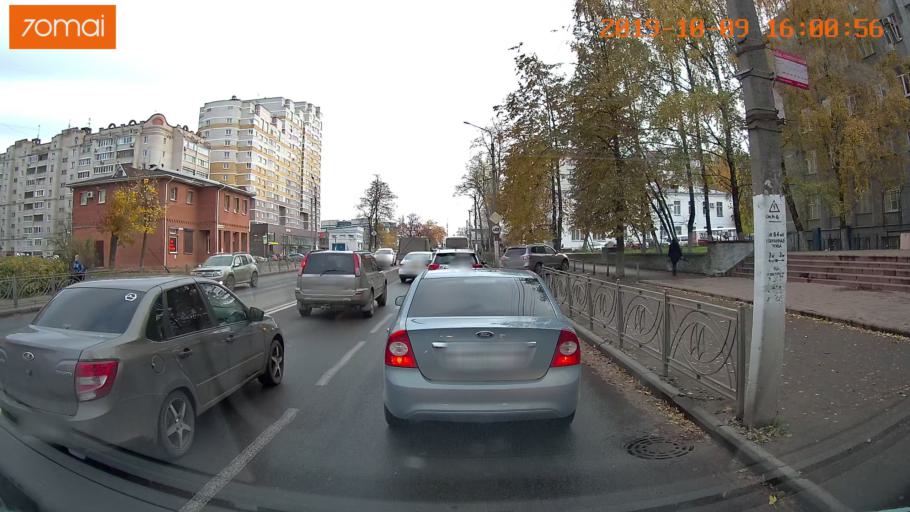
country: RU
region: Kostroma
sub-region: Kostromskoy Rayon
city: Kostroma
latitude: 57.7656
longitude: 40.9511
